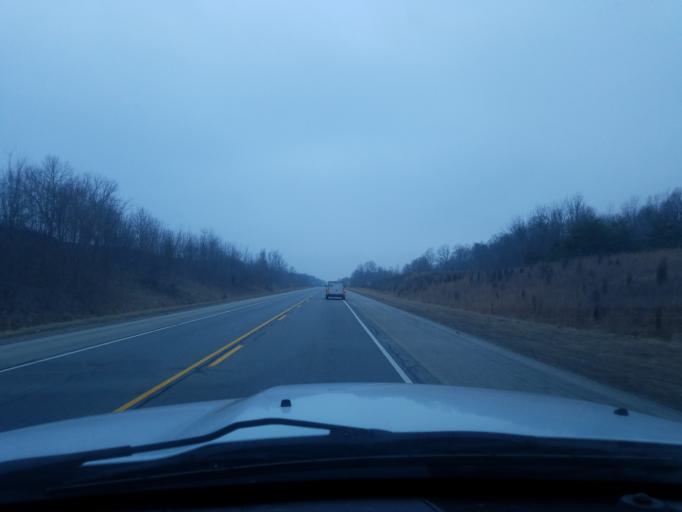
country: US
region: Indiana
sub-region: Perry County
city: Tell City
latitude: 37.9919
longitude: -86.7079
